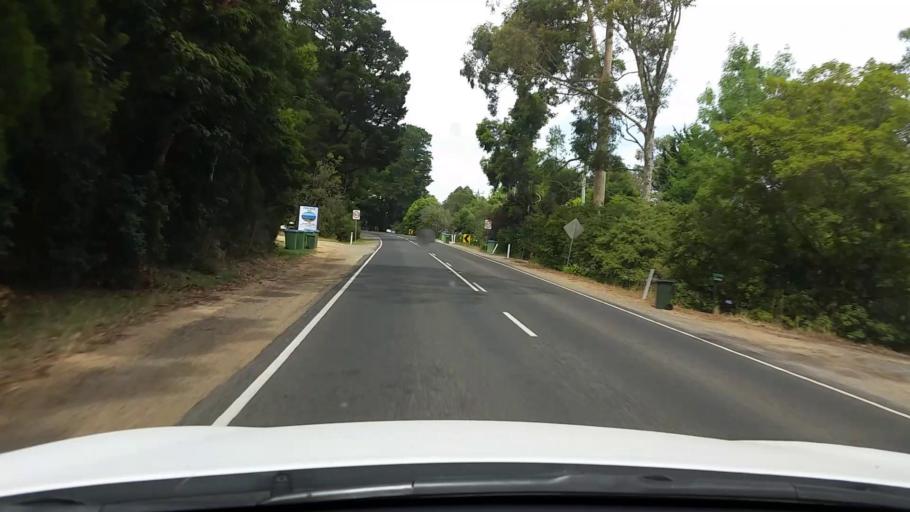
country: AU
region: Victoria
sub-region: Mornington Peninsula
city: Merricks
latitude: -38.3923
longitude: 145.0860
